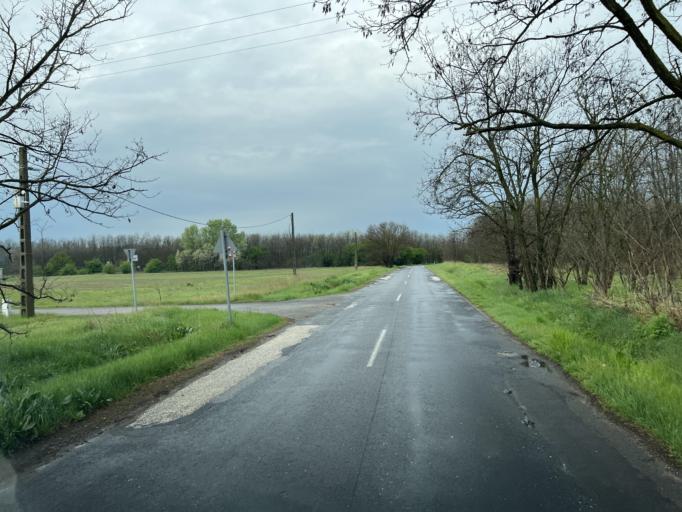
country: HU
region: Pest
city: Ujhartyan
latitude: 47.2321
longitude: 19.4379
